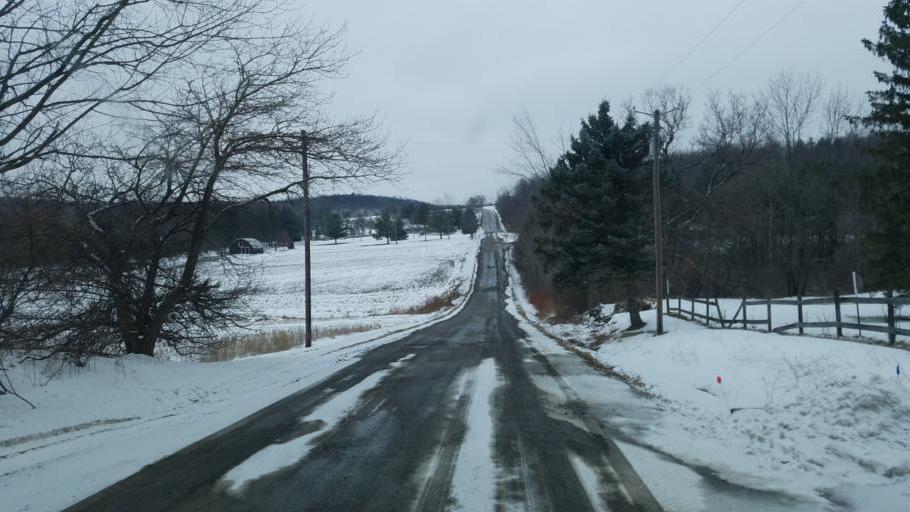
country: US
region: Pennsylvania
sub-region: Tioga County
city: Elkland
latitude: 42.1119
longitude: -77.4007
